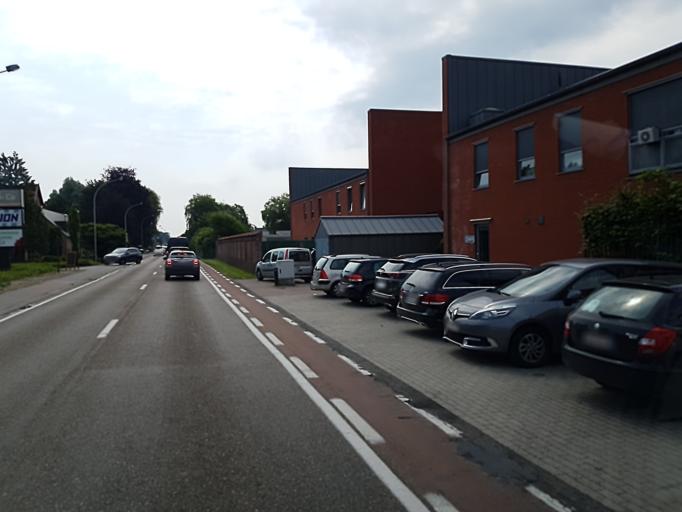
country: BE
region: Flanders
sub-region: Provincie Antwerpen
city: Mol
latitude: 51.1827
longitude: 5.1176
